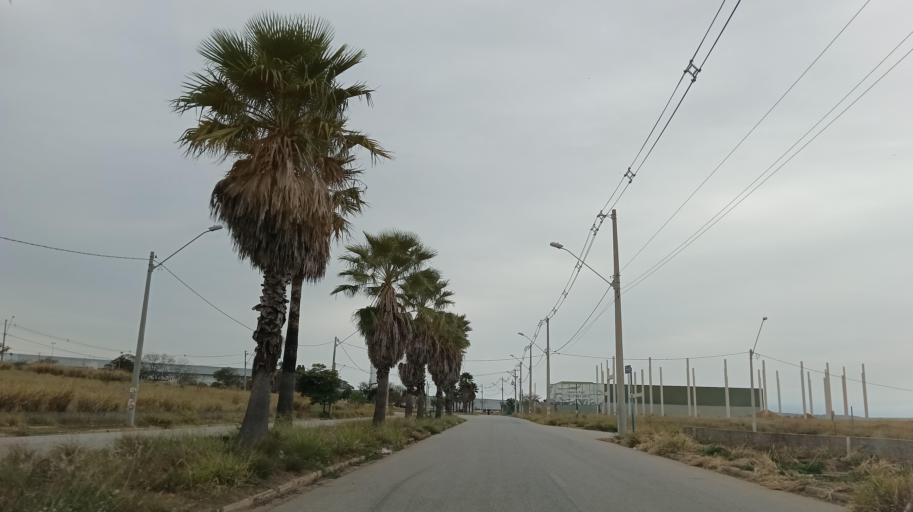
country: BR
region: Sao Paulo
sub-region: Sorocaba
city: Sorocaba
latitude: -23.4589
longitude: -47.4546
